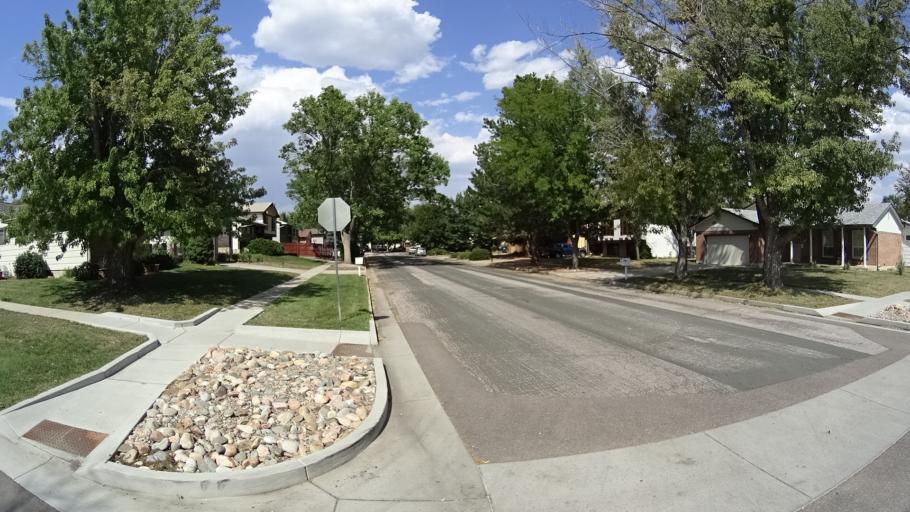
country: US
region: Colorado
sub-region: El Paso County
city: Colorado Springs
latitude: 38.8487
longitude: -104.7646
